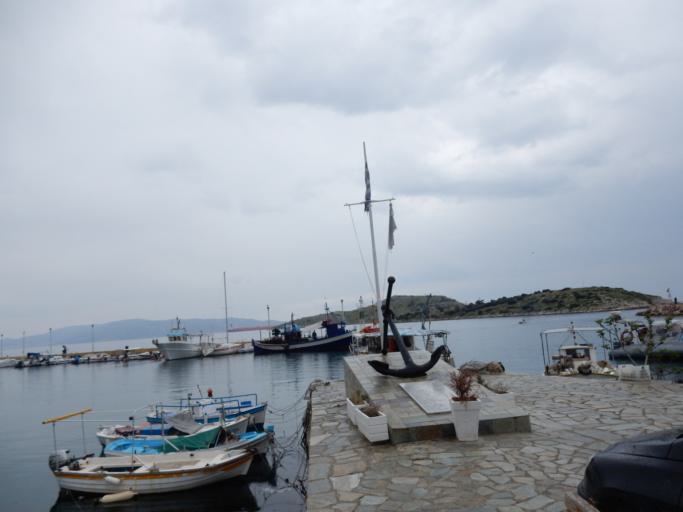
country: GR
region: Attica
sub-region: Nomarchia Dytikis Attikis
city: Megara
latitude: 37.9737
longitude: 23.3617
